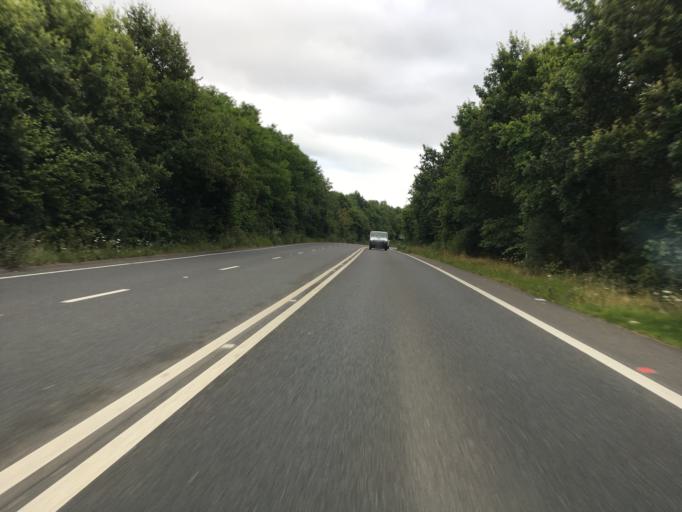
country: GB
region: England
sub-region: Hampshire
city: Petersfield
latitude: 51.0146
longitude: -0.9253
